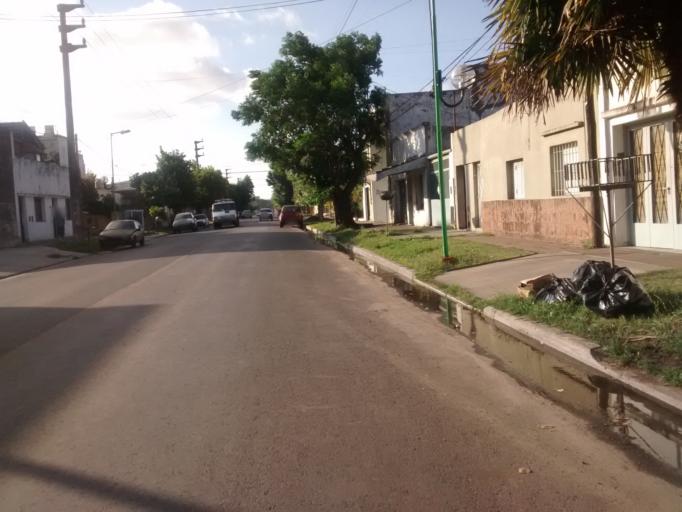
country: AR
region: Buenos Aires
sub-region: Partido de La Plata
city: La Plata
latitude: -34.9409
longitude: -57.9284
